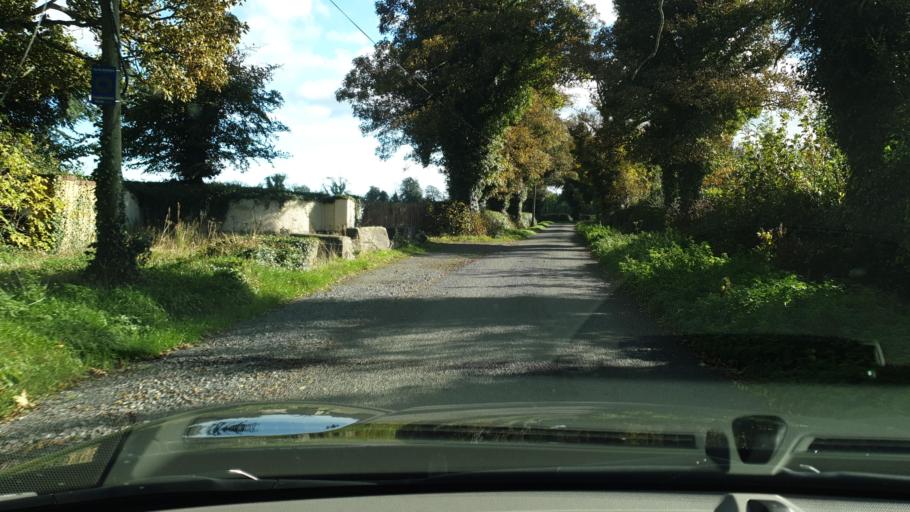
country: IE
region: Leinster
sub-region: Fingal County
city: Swords
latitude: 53.4927
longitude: -6.2660
